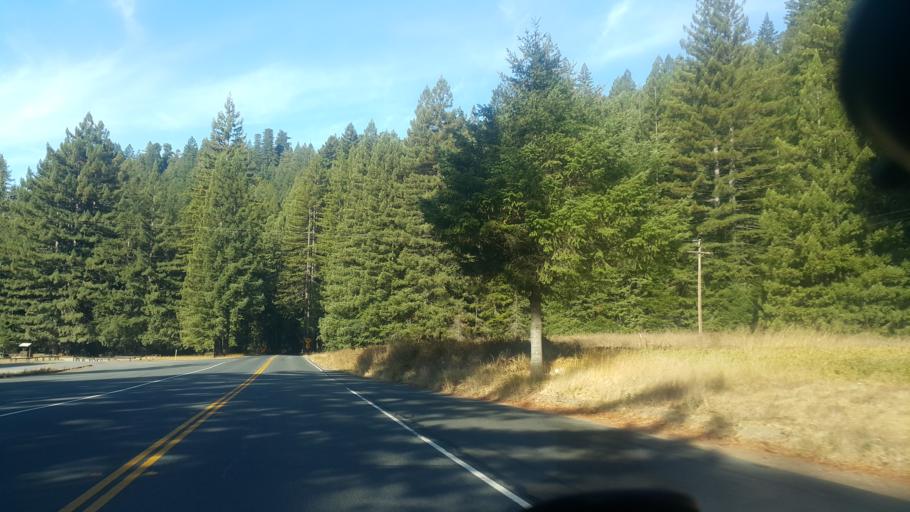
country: US
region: California
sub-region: Mendocino County
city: Brooktrails
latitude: 39.3527
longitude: -123.5580
